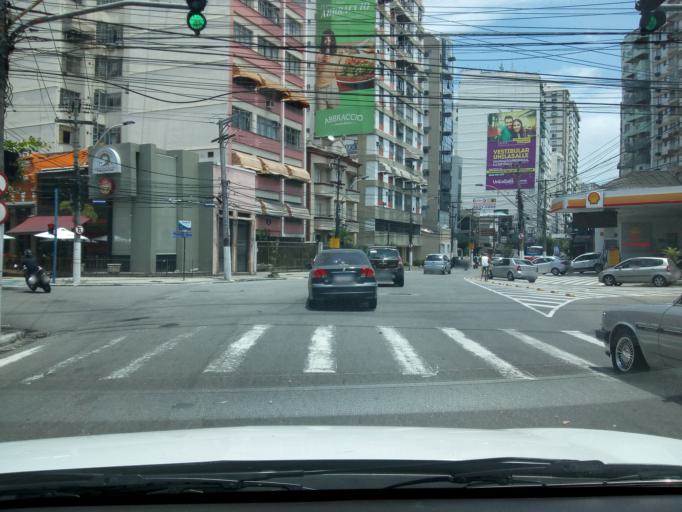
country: BR
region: Rio de Janeiro
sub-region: Niteroi
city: Niteroi
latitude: -22.8999
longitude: -43.1122
